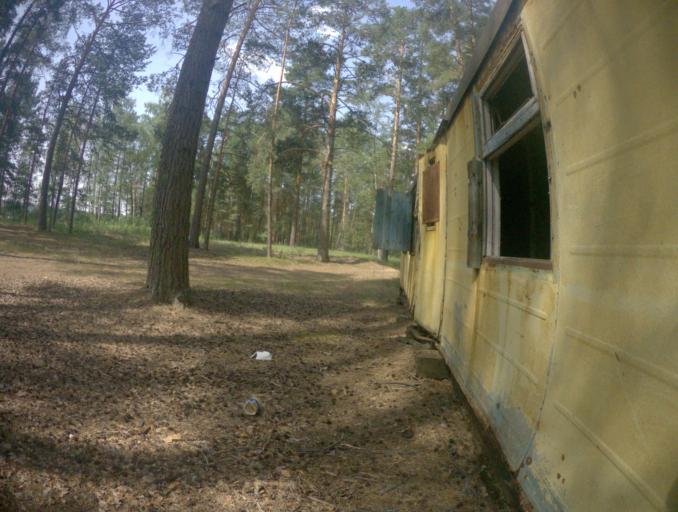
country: RU
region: Ivanovo
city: Talitsy
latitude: 56.3974
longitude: 42.3975
